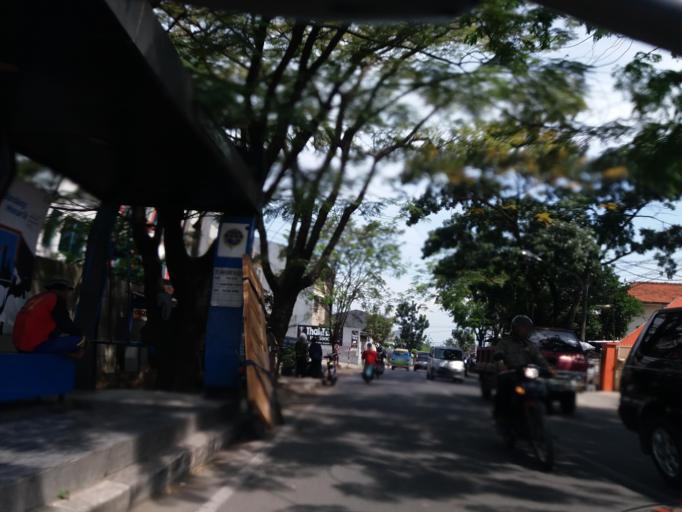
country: ID
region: West Java
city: Margahayukencana
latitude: -6.9376
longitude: 107.5701
